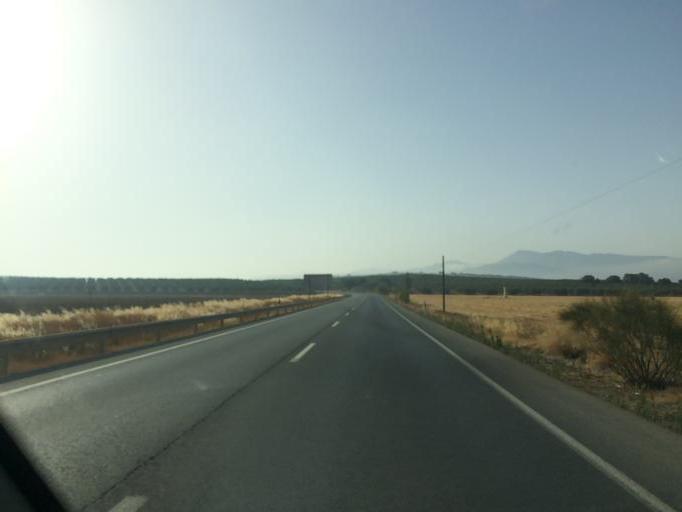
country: ES
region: Andalusia
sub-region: Provincia de Malaga
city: Humilladero
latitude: 37.0613
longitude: -4.6955
